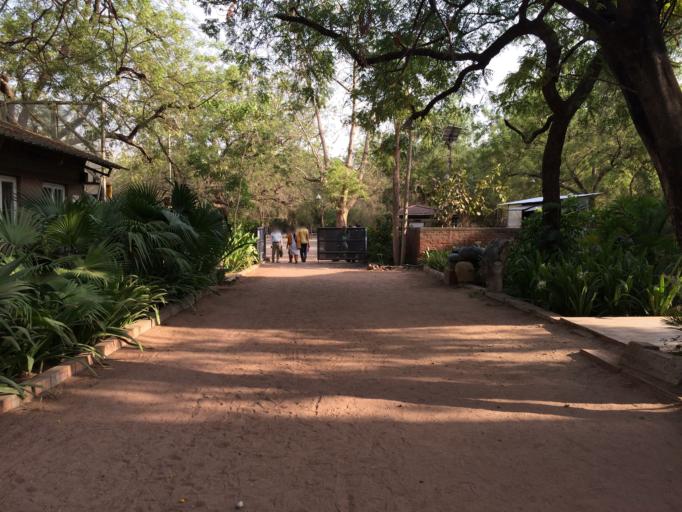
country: IN
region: Gujarat
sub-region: Ahmadabad
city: Ahmedabad
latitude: 23.0368
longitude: 72.5503
